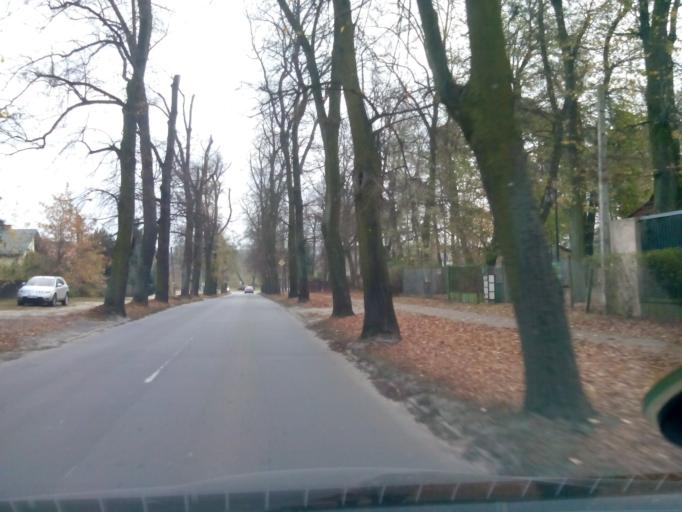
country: PL
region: Masovian Voivodeship
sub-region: Powiat pruszkowski
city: Komorow
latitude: 52.1453
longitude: 20.8242
